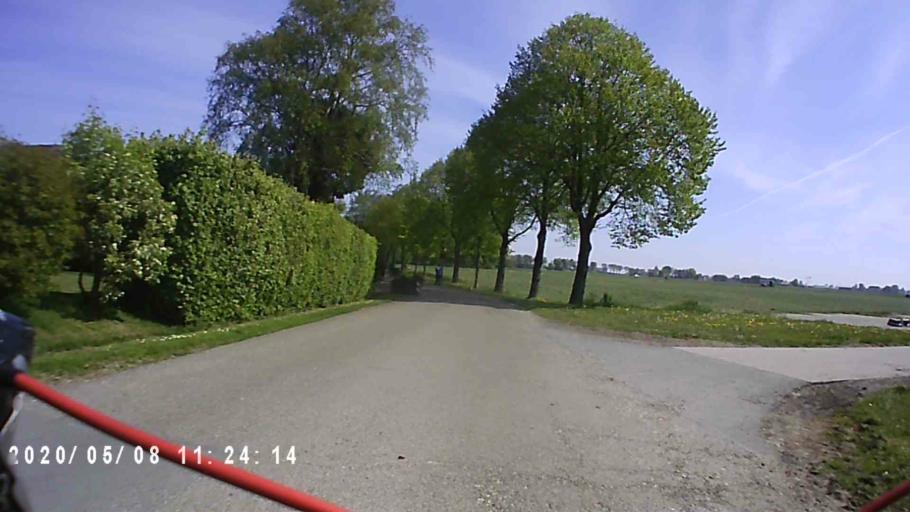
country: NL
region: Groningen
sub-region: Gemeente Bedum
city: Bedum
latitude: 53.3448
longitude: 6.6760
